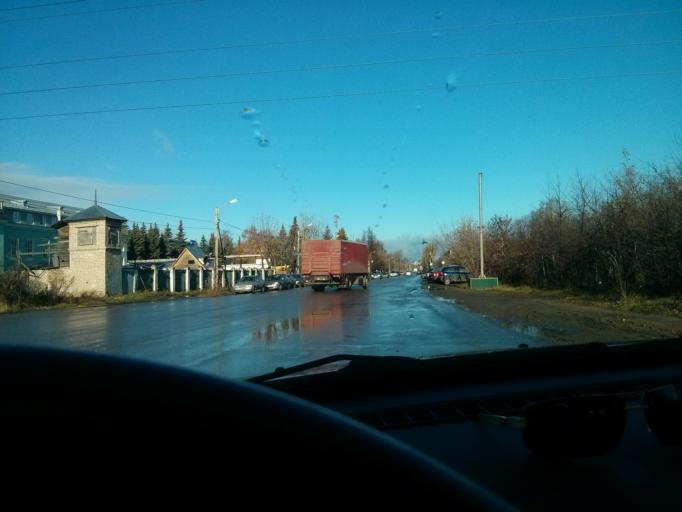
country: RU
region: Vladimir
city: Murom
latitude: 55.5516
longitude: 42.0487
